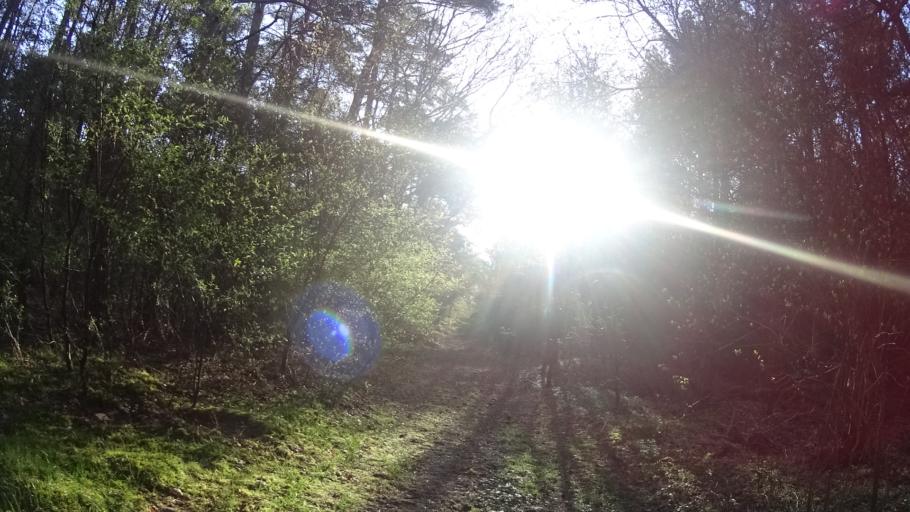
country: DE
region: Lower Saxony
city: Haren
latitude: 52.8154
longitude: 7.2634
